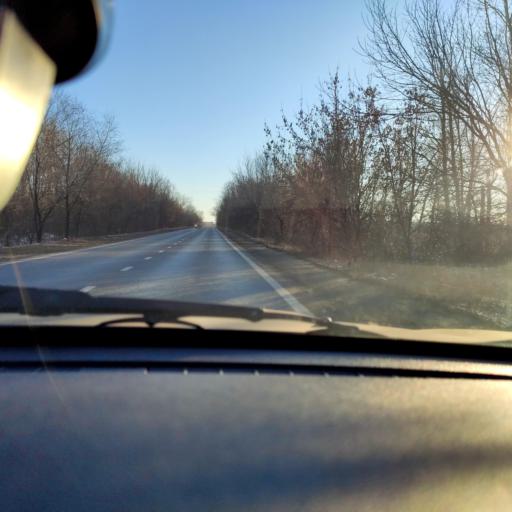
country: RU
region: Samara
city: Tol'yatti
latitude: 53.5488
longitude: 49.3937
